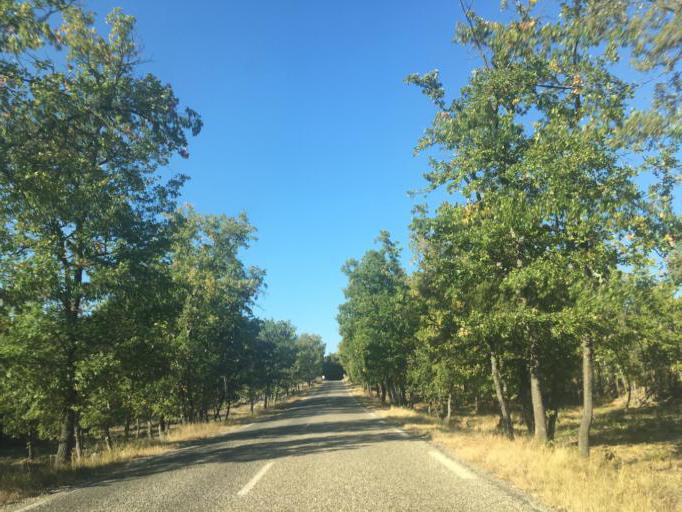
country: FR
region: Provence-Alpes-Cote d'Azur
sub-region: Departement du Var
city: Aups
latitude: 43.6093
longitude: 6.2188
